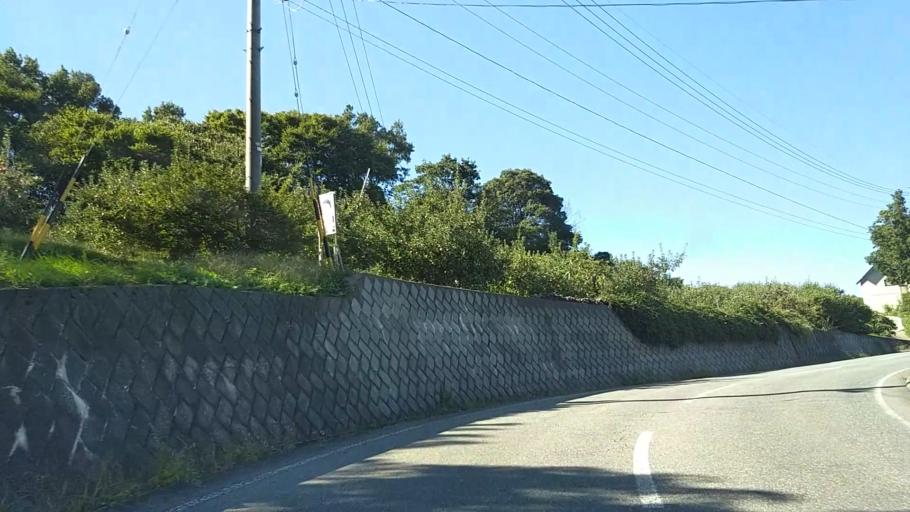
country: JP
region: Nagano
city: Nagano-shi
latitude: 36.5821
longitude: 138.1110
